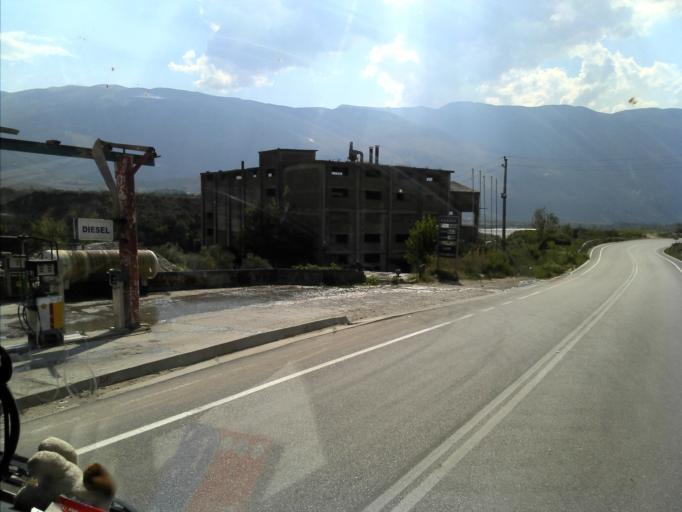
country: AL
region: Gjirokaster
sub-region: Rrethi i Tepelenes
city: Memaliaj
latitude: 40.3532
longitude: 19.9700
